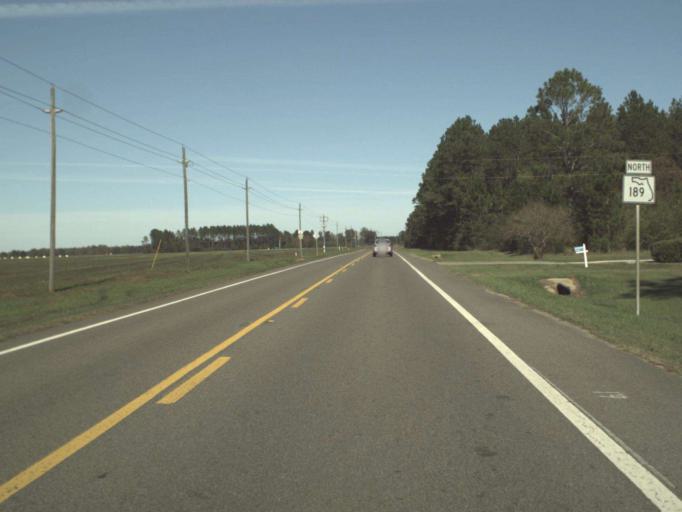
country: US
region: Florida
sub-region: Okaloosa County
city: Crestview
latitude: 30.8187
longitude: -86.6770
